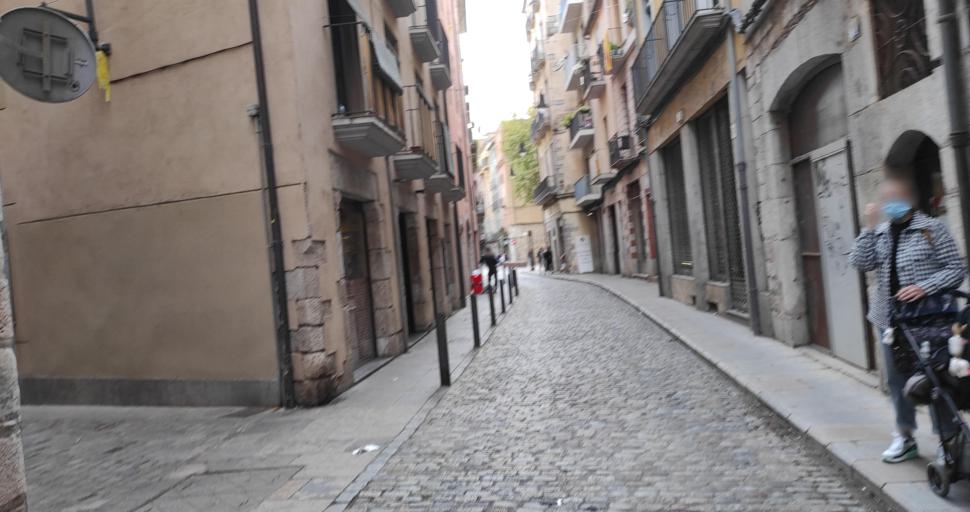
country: ES
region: Catalonia
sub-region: Provincia de Girona
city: Girona
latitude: 41.9887
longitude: 2.8244
